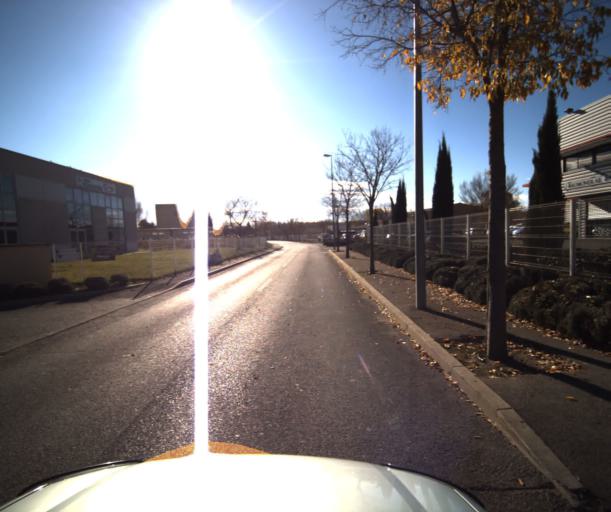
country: FR
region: Provence-Alpes-Cote d'Azur
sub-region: Departement du Vaucluse
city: Pertuis
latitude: 43.6770
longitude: 5.5032
